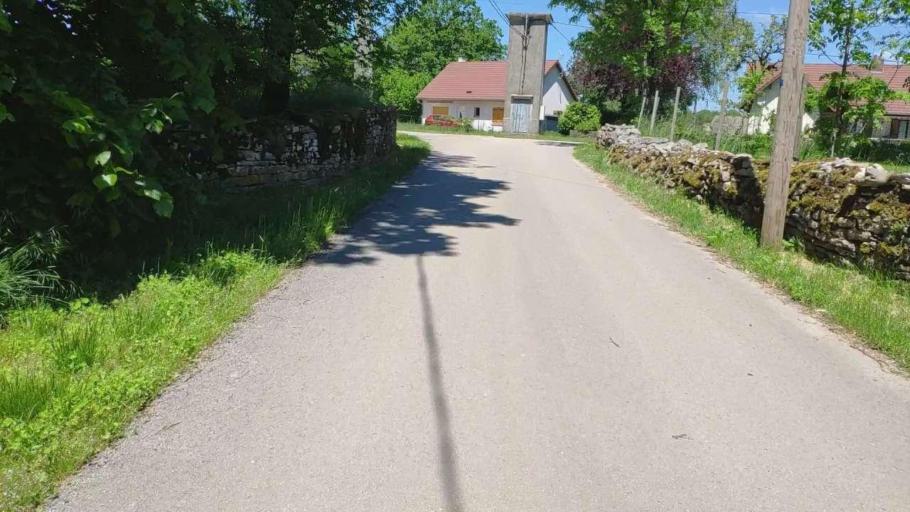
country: FR
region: Franche-Comte
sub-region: Departement du Jura
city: Poligny
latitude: 46.7370
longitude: 5.7007
